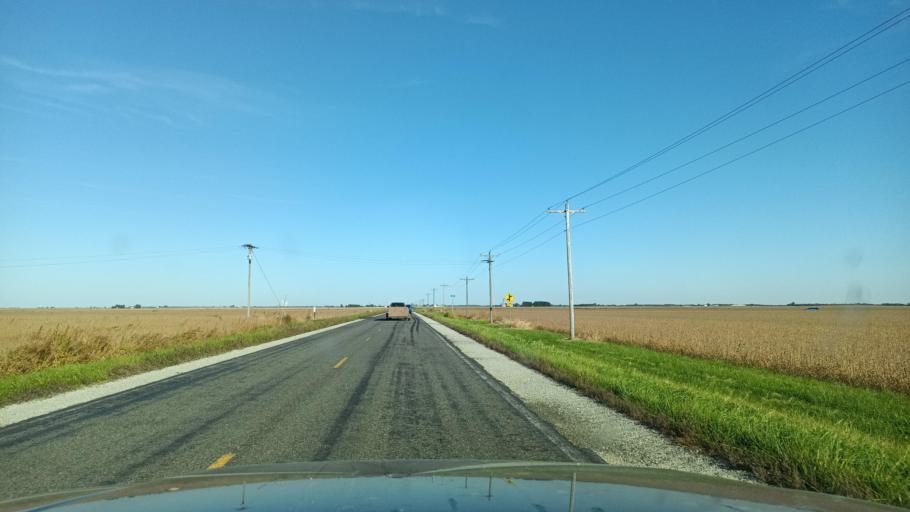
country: US
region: Illinois
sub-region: McLean County
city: Le Roy
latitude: 40.2243
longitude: -88.7859
